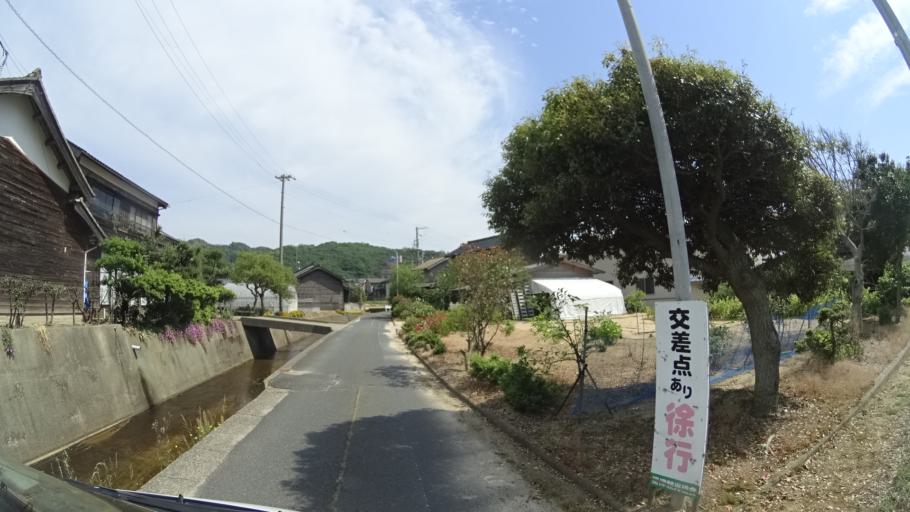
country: JP
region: Kyoto
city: Miyazu
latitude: 35.7002
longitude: 135.0540
